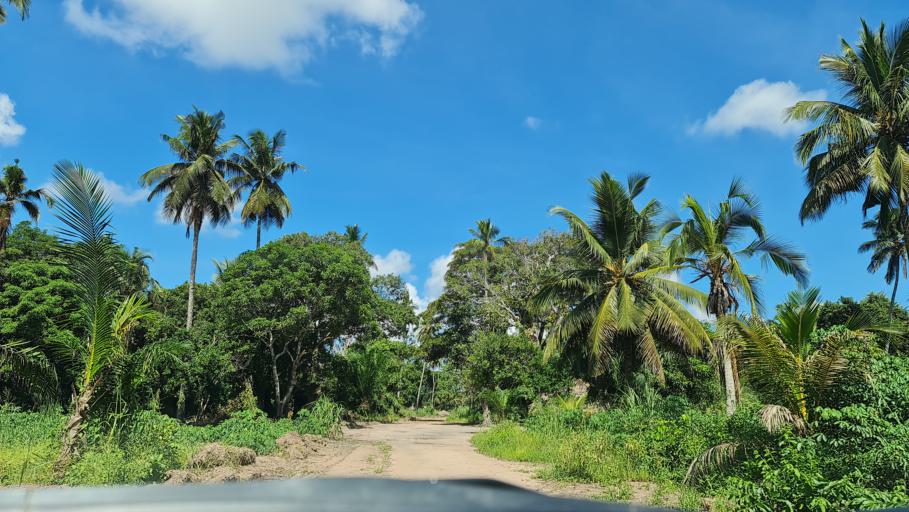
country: MZ
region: Zambezia
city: Quelimane
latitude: -17.3844
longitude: 37.5272
